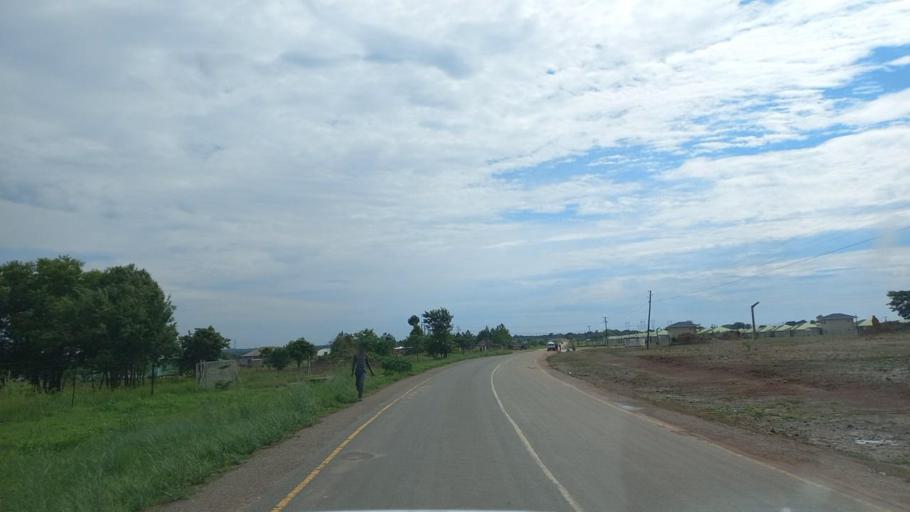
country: ZM
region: Copperbelt
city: Kitwe
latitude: -12.8732
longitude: 28.3324
